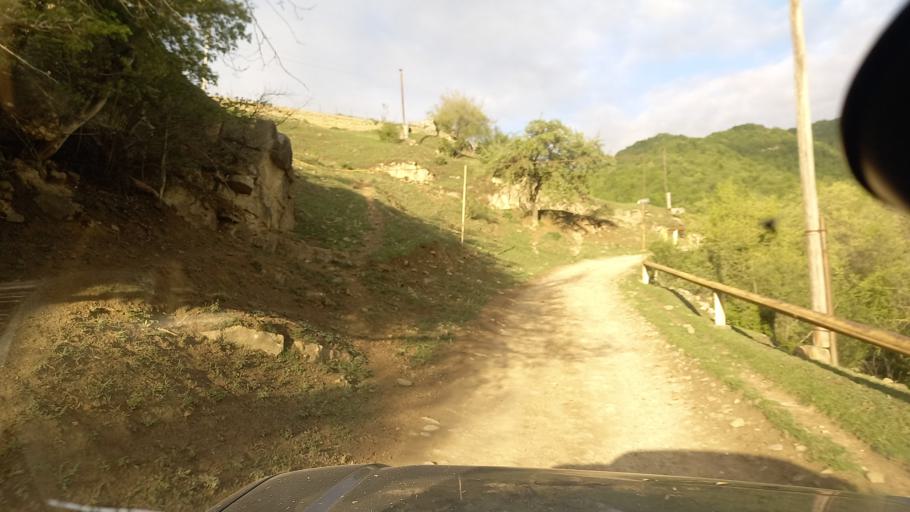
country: RU
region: Dagestan
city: Khuchni
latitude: 41.9481
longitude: 47.8343
